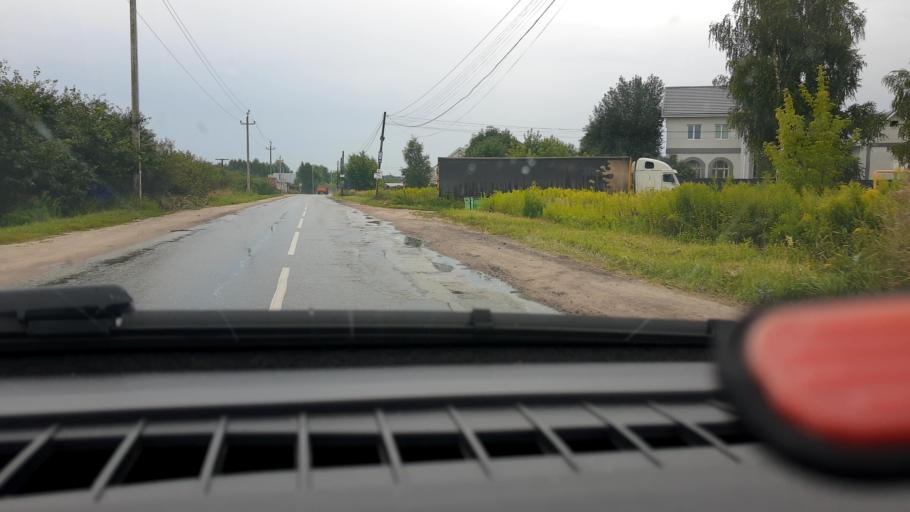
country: RU
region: Nizjnij Novgorod
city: Bor
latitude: 56.3524
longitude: 44.1227
